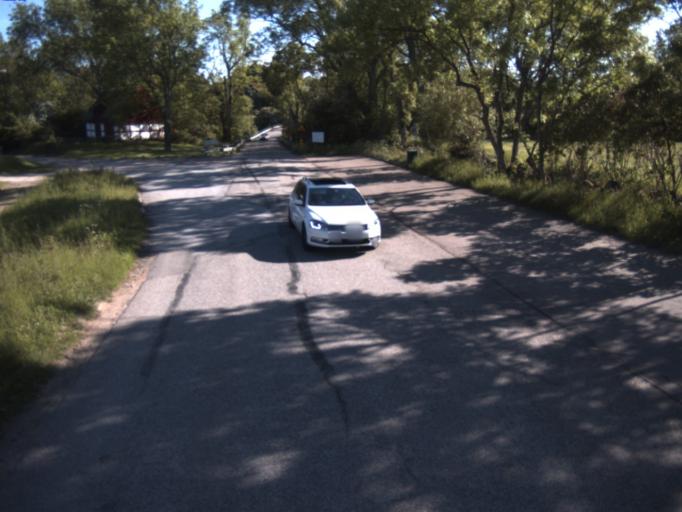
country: SE
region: Skane
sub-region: Helsingborg
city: Rydeback
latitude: 56.0011
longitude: 12.7636
